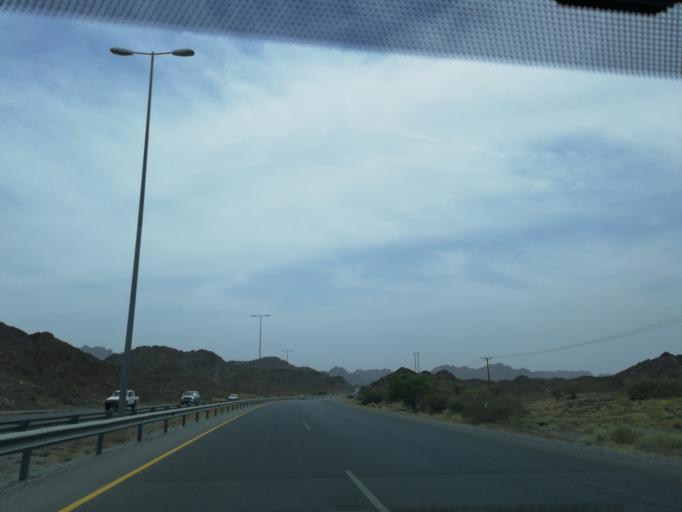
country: OM
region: Muhafazat ad Dakhiliyah
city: Izki
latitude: 22.9480
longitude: 57.7896
